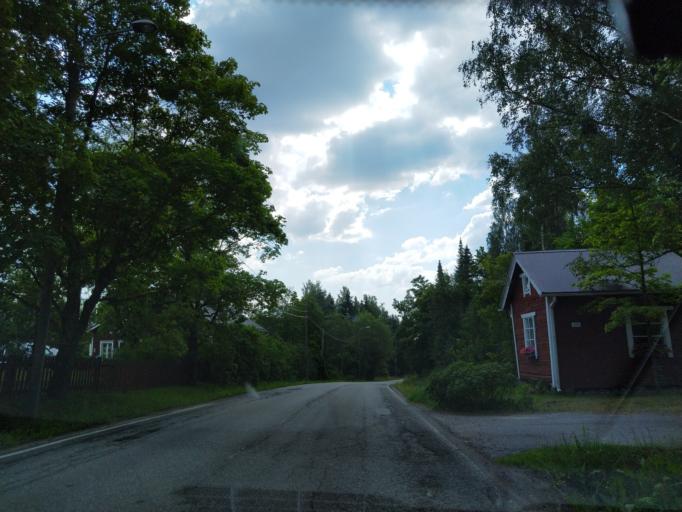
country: FI
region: Uusimaa
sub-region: Helsinki
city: Kirkkonummi
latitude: 60.1037
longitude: 24.4858
